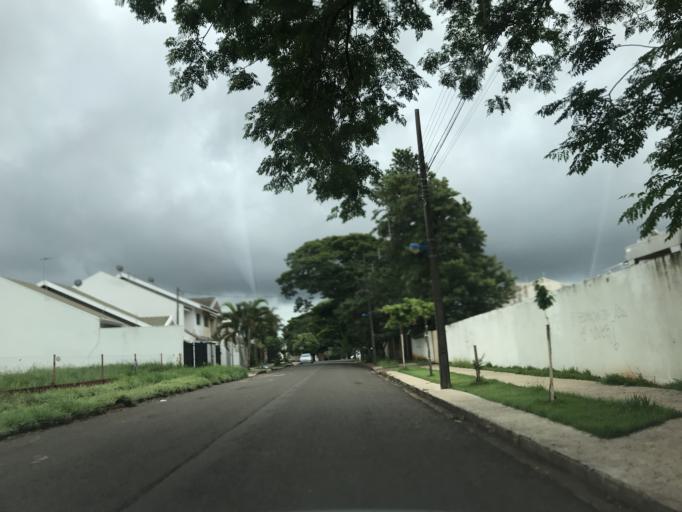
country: BR
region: Parana
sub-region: Maringa
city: Maringa
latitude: -23.4456
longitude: -51.9573
